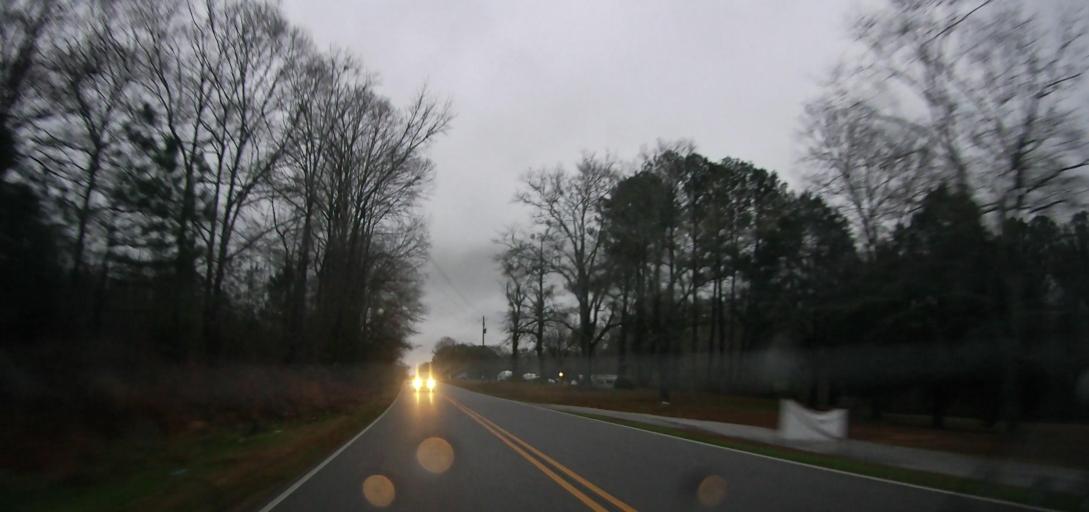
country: US
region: Alabama
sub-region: Tuscaloosa County
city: Vance
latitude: 33.1152
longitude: -87.2198
